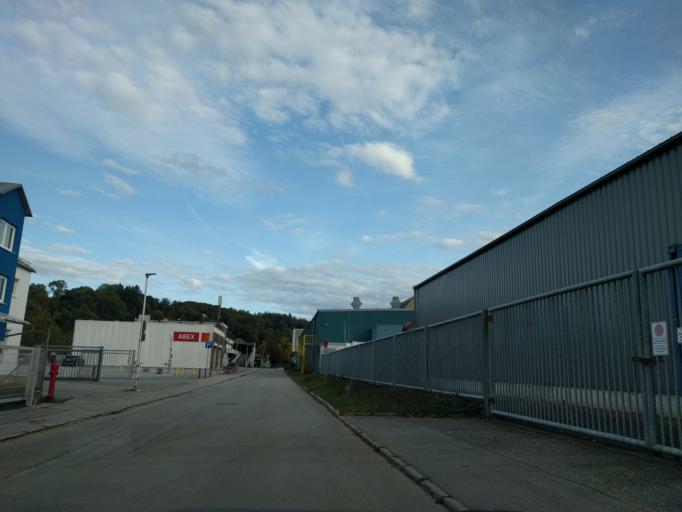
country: DE
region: Bavaria
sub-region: Lower Bavaria
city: Deggendorf
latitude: 48.8283
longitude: 12.9578
